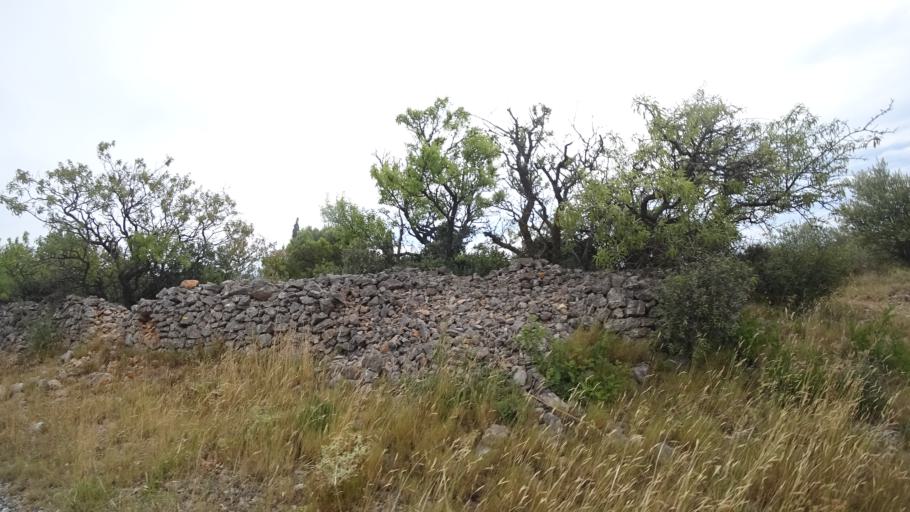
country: FR
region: Languedoc-Roussillon
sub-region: Departement de l'Aude
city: Leucate
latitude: 42.9056
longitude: 3.0270
